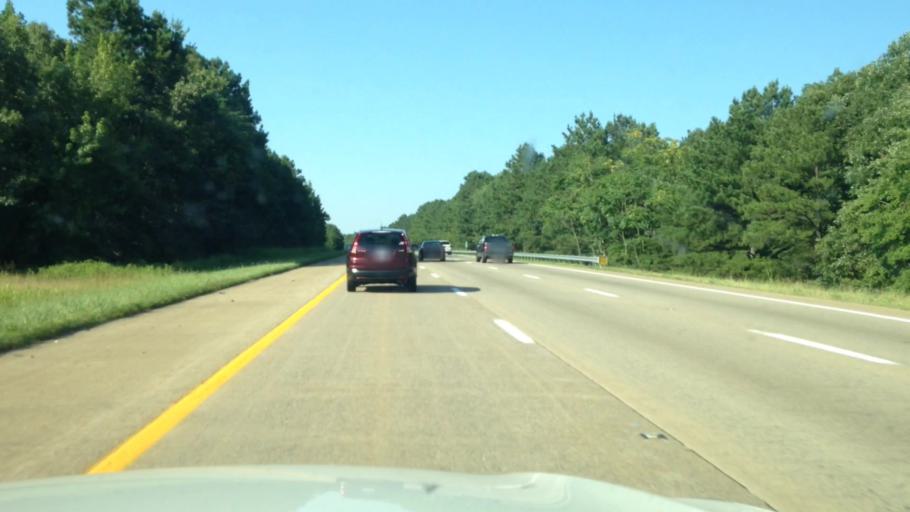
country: US
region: Virginia
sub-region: Henrico County
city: Fort Lee
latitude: 37.4571
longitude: -77.3163
